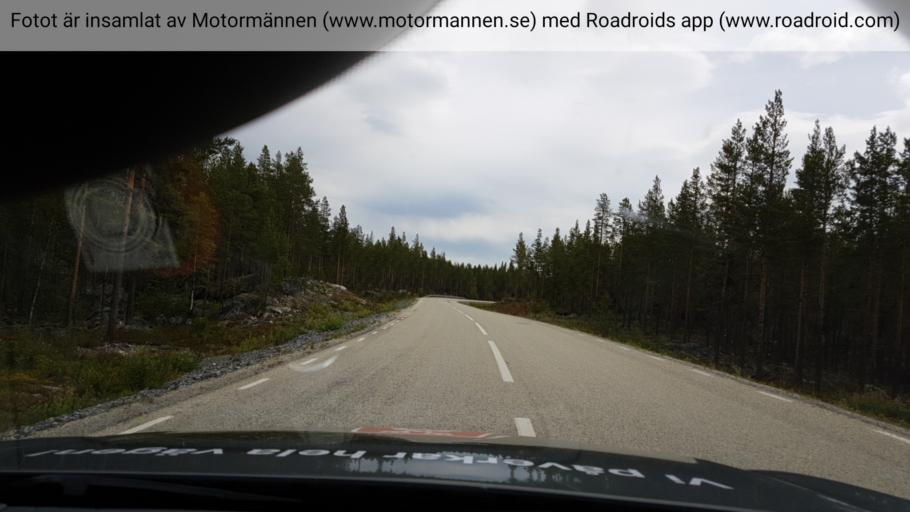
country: SE
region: Jaemtland
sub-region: Are Kommun
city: Jarpen
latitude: 62.8439
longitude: 13.4044
